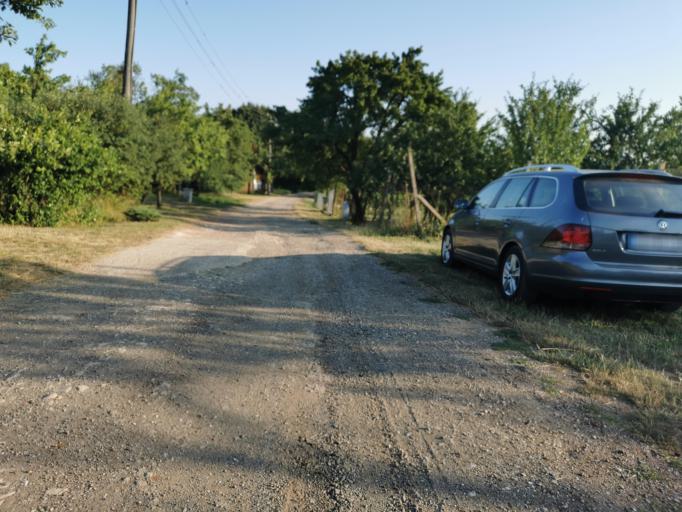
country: CZ
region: South Moravian
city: Sudomerice
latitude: 48.8026
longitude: 17.2918
